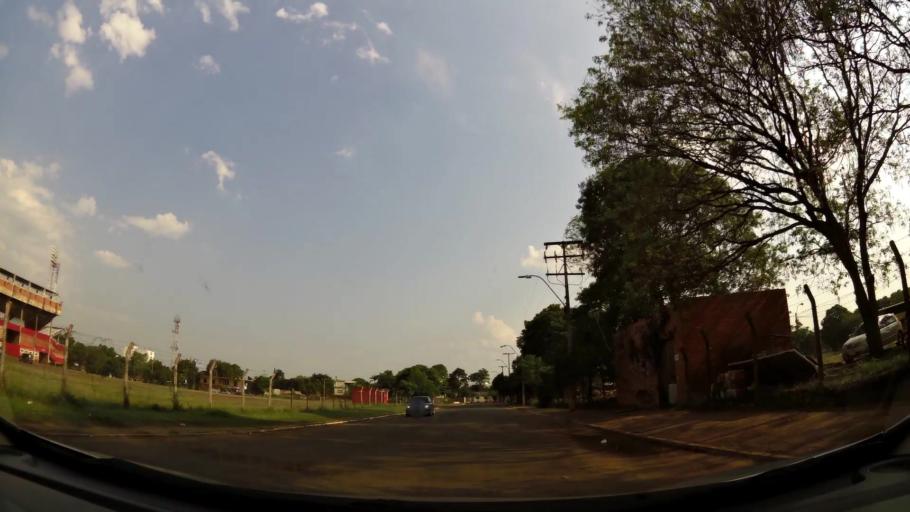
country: PY
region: Alto Parana
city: Presidente Franco
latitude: -25.5269
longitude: -54.6139
